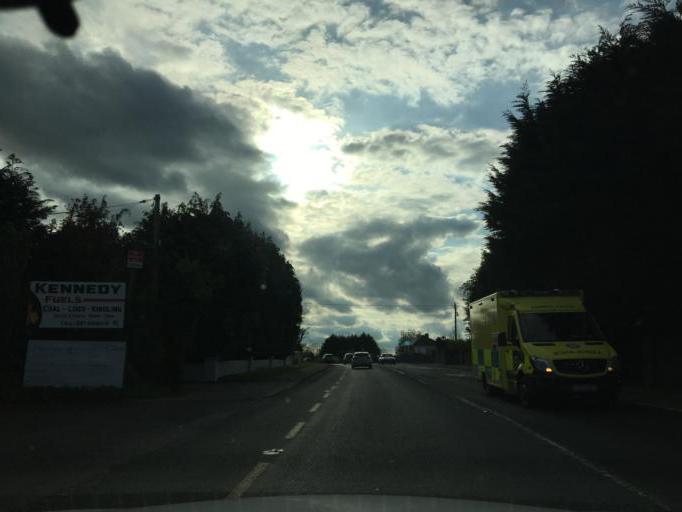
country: IE
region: Leinster
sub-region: Loch Garman
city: Loch Garman
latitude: 52.3414
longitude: -6.4973
